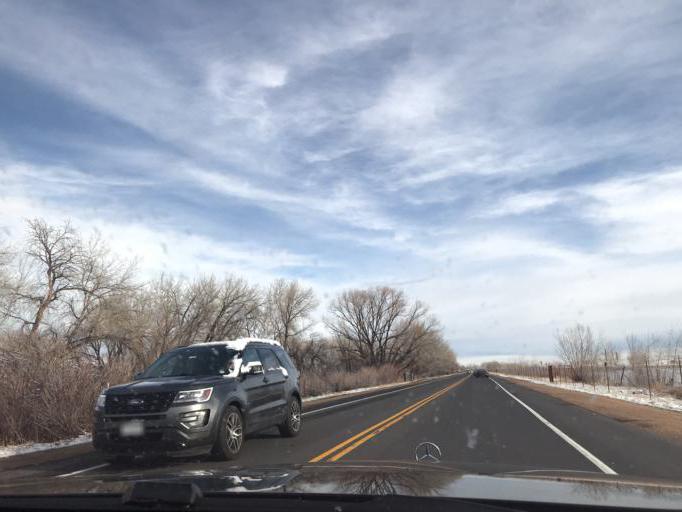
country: US
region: Colorado
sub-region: Boulder County
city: Superior
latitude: 39.9905
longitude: -105.2127
